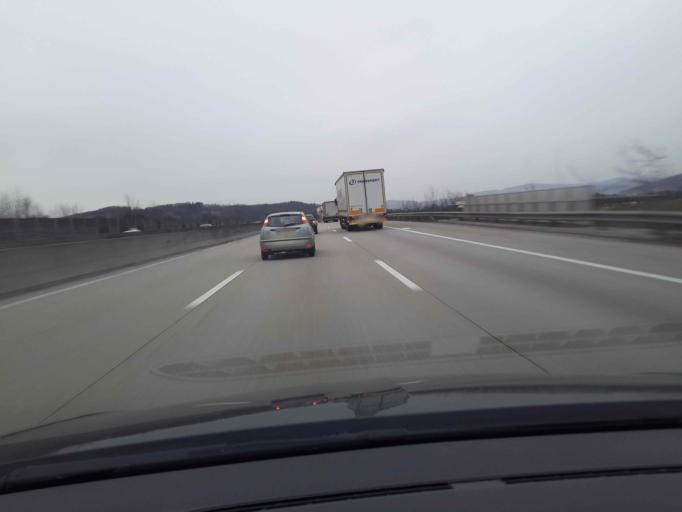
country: AT
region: Upper Austria
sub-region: Politischer Bezirk Linz-Land
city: Sankt Florian
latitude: 48.2294
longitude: 14.3847
